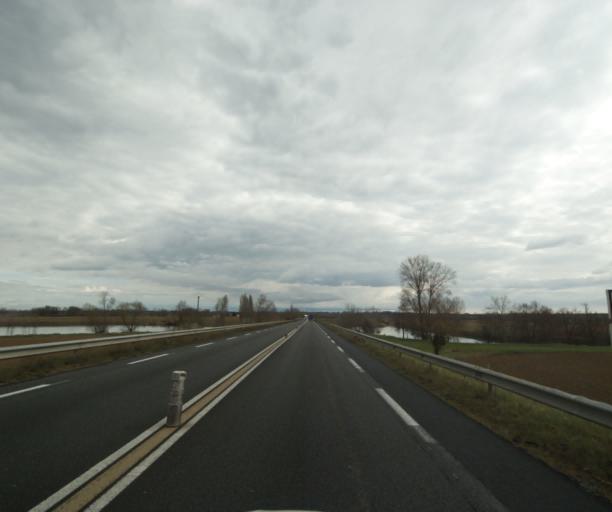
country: FR
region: Auvergne
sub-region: Departement de l'Allier
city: Toulon-sur-Allier
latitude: 46.4825
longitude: 3.3341
